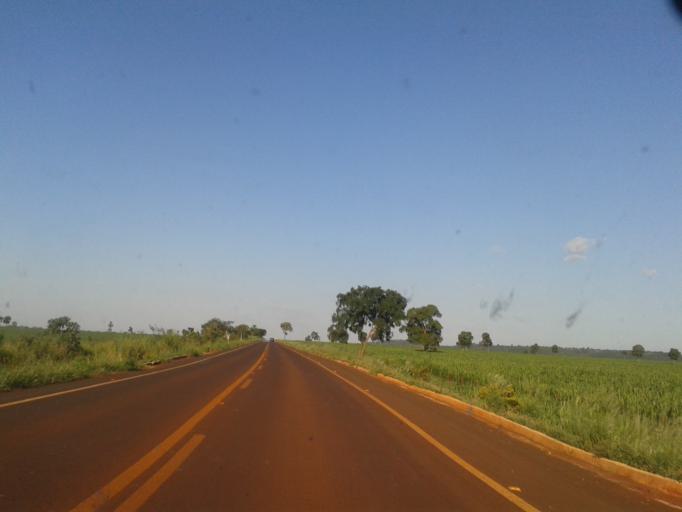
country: BR
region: Minas Gerais
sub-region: Capinopolis
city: Capinopolis
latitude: -18.7122
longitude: -49.8419
